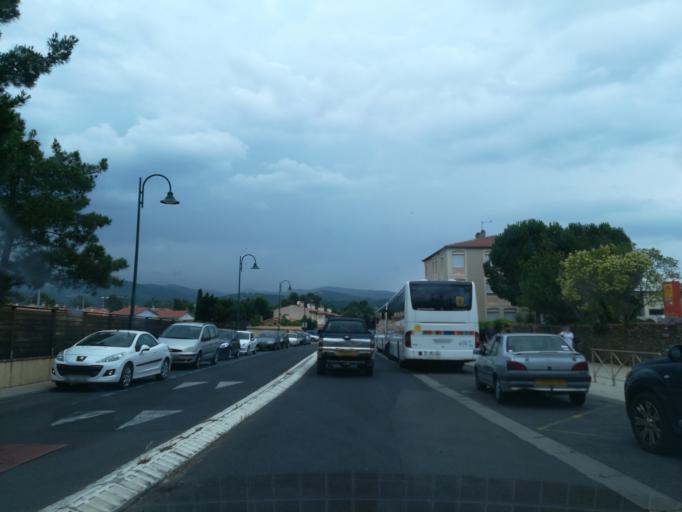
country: FR
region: Languedoc-Roussillon
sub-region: Departement des Pyrenees-Orientales
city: Ceret
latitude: 42.4862
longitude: 2.7540
